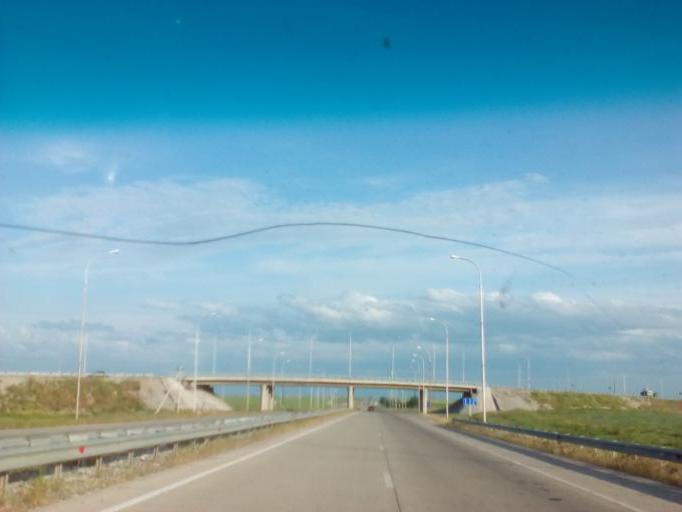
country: KZ
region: Ongtustik Qazaqstan
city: Temirlanovka
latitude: 42.5501
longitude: 69.3217
